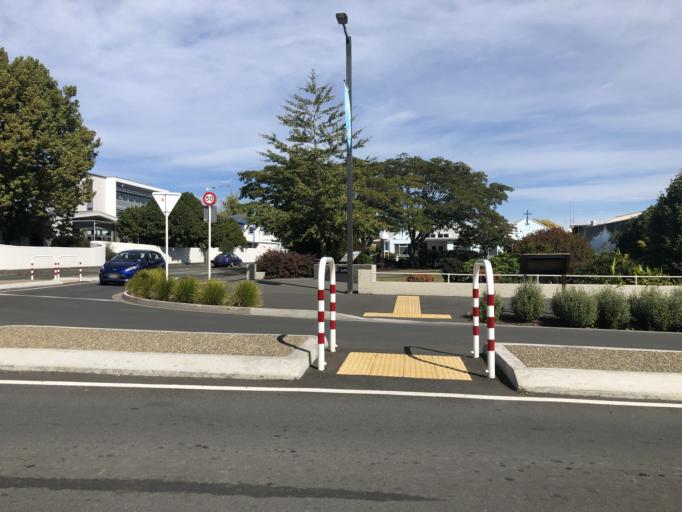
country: NZ
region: Tasman
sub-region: Tasman District
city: Richmond
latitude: -41.3410
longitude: 173.1867
